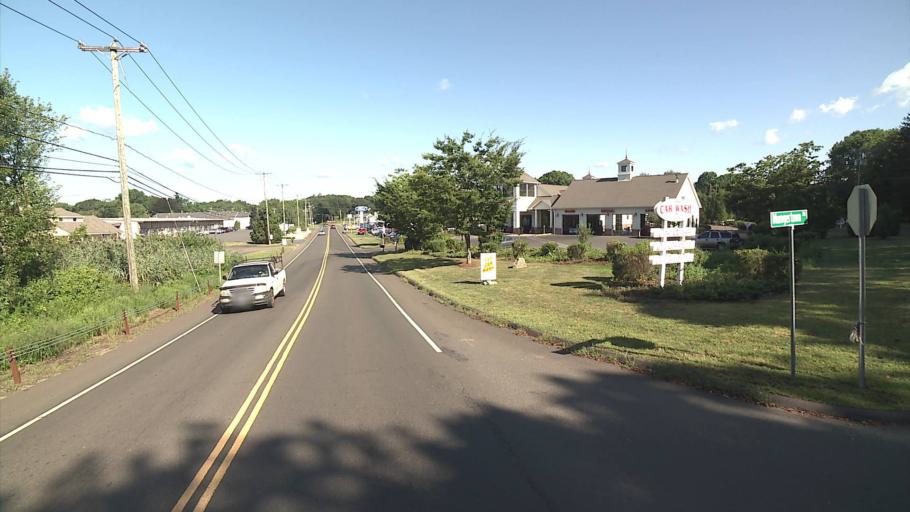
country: US
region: Connecticut
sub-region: New Haven County
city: Madison Center
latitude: 41.2804
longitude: -72.6295
